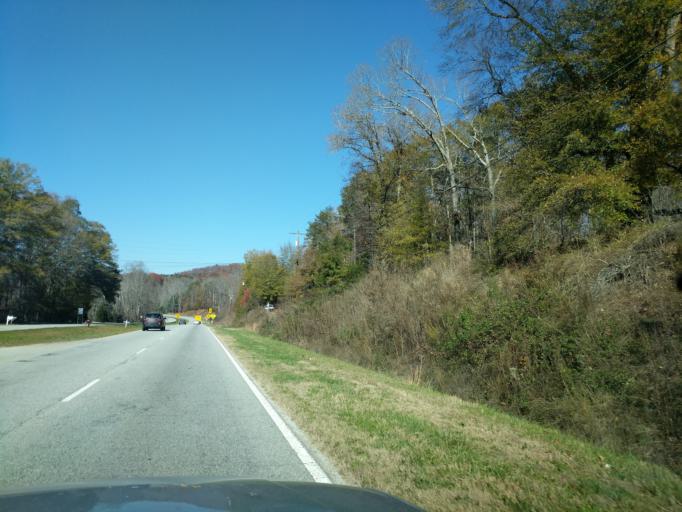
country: US
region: South Carolina
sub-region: Greenville County
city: Tigerville
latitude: 35.0578
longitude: -82.4271
